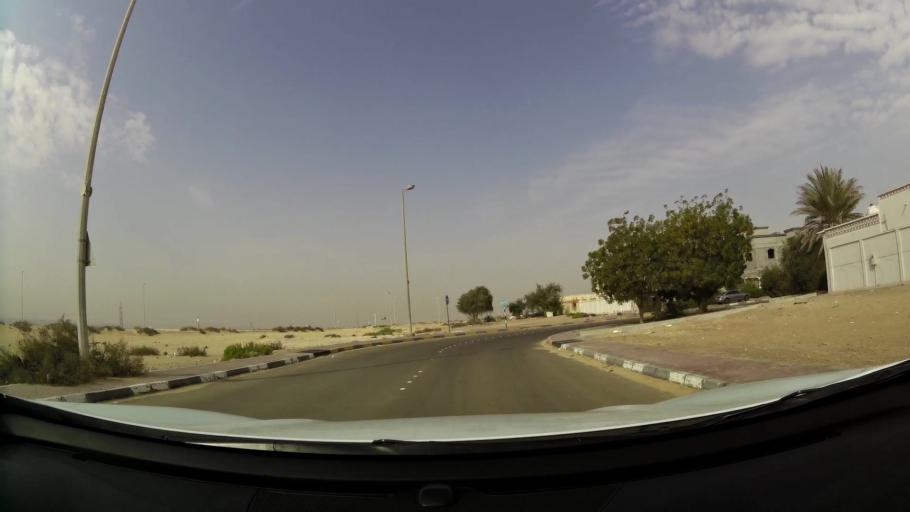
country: AE
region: Abu Dhabi
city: Abu Dhabi
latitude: 24.2603
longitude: 54.7012
